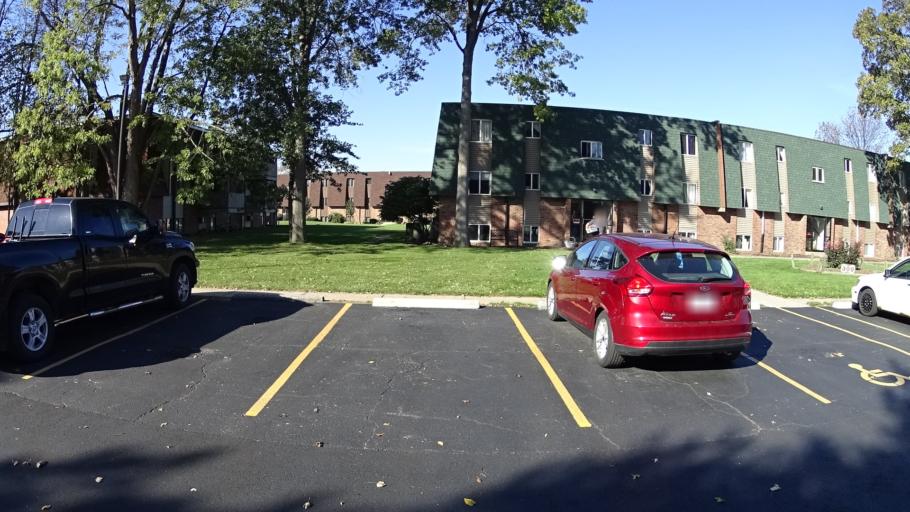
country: US
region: Ohio
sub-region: Lorain County
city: Vermilion
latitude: 41.4277
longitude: -82.3479
